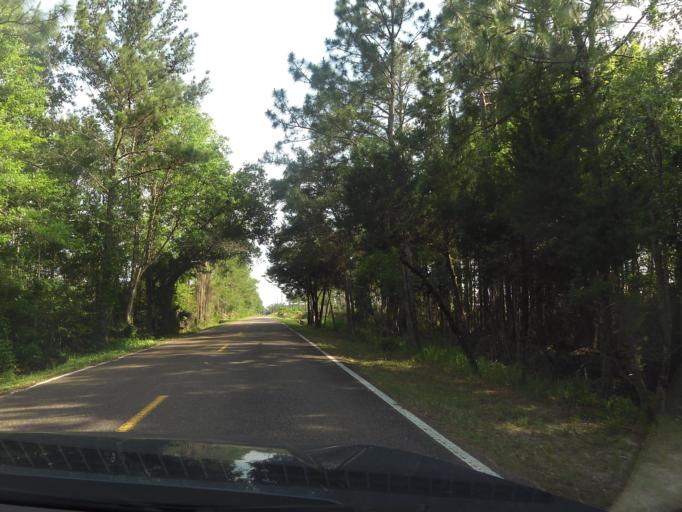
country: US
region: Florida
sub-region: Duval County
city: Atlantic Beach
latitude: 30.4747
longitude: -81.4866
